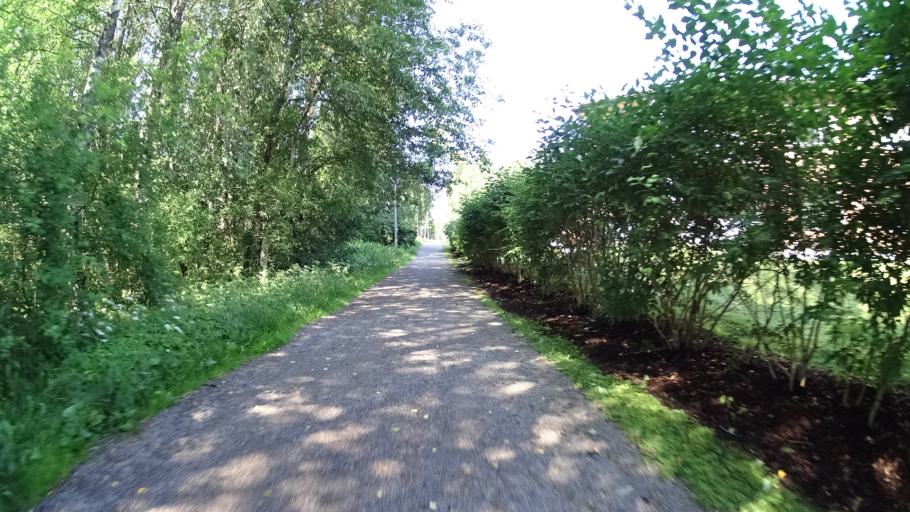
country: FI
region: Uusimaa
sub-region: Helsinki
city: Kilo
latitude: 60.2281
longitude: 24.7811
